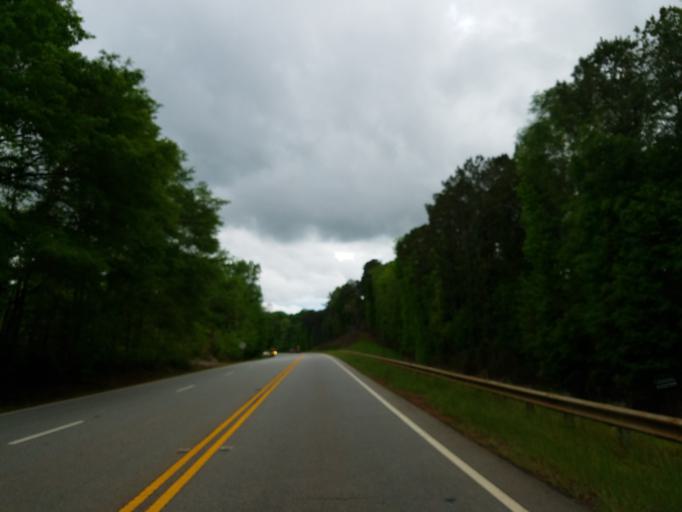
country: US
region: Georgia
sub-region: Lamar County
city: Barnesville
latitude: 32.9041
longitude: -84.0774
